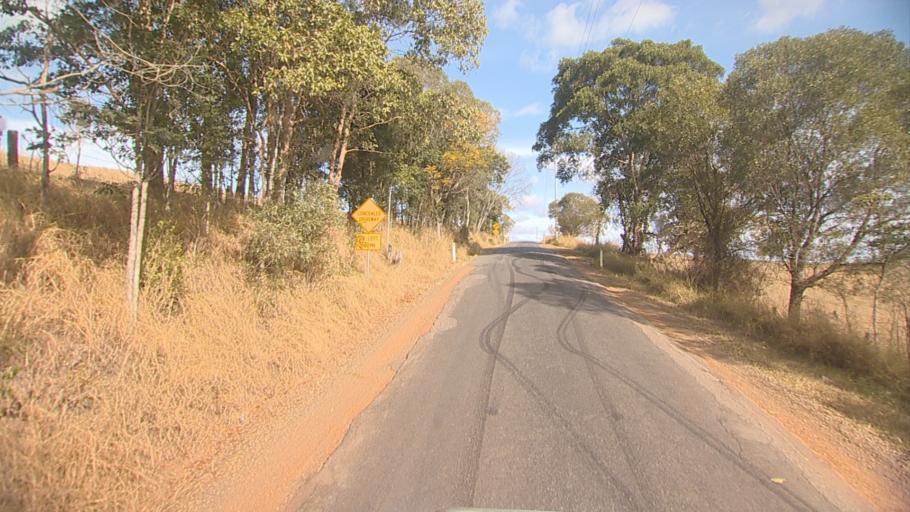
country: AU
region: Queensland
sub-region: Logan
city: Cedar Vale
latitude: -27.9030
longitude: 153.0148
